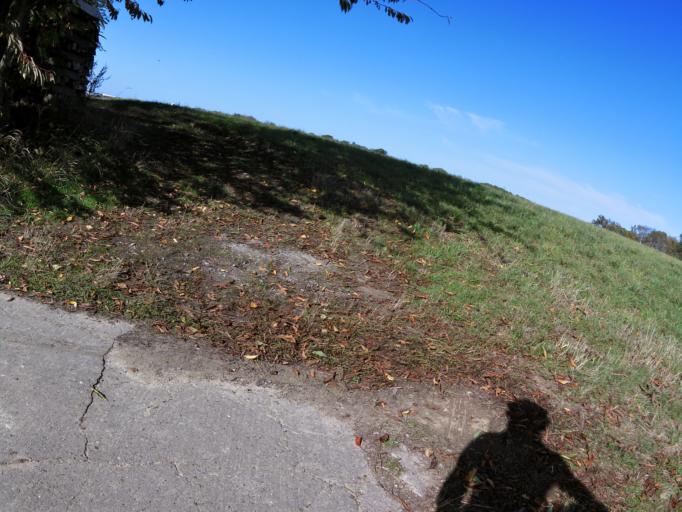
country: DE
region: Bavaria
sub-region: Regierungsbezirk Unterfranken
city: Biebelried
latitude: 49.7653
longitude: 10.0896
